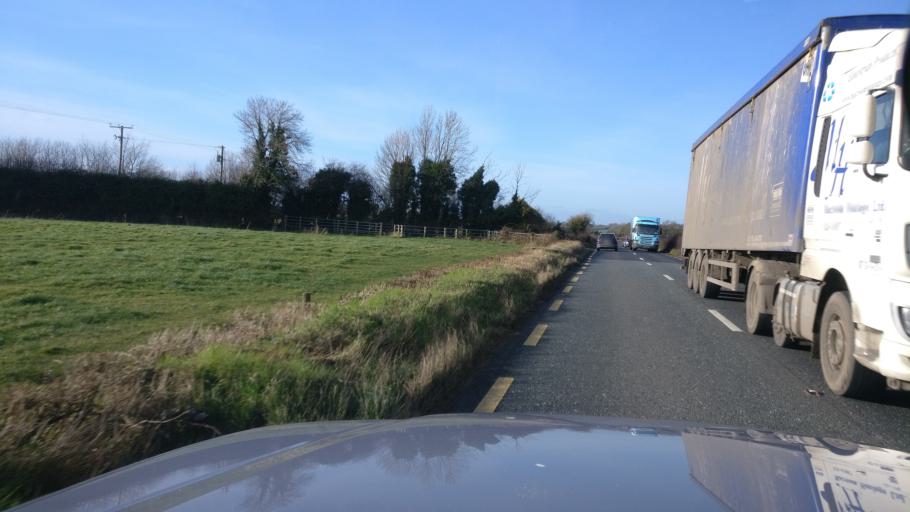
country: IE
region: Leinster
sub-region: Laois
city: Mountmellick
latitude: 53.1833
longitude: -7.3978
